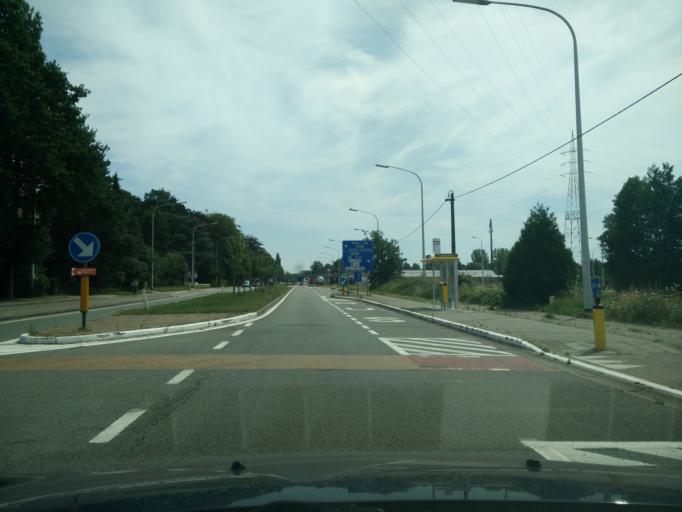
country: BE
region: Flanders
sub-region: Provincie Oost-Vlaanderen
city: Melle
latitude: 51.0141
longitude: 3.7861
